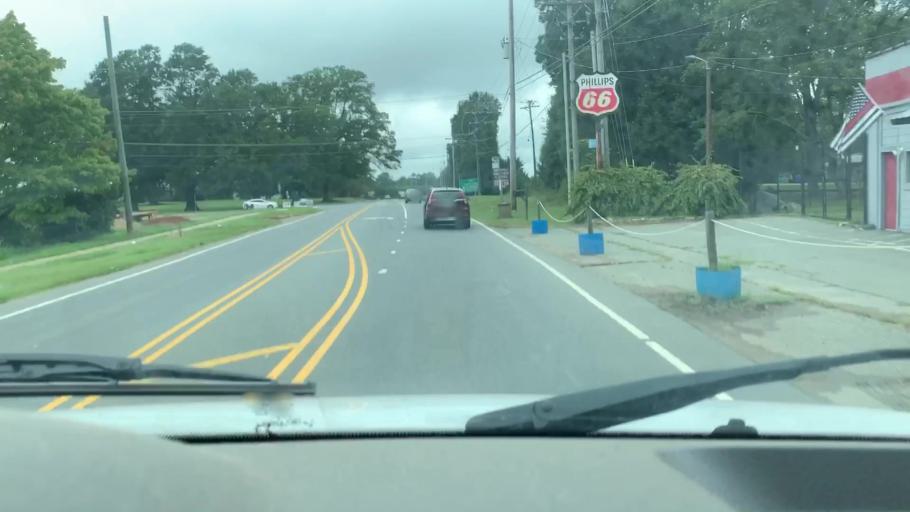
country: US
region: North Carolina
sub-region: Mecklenburg County
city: Huntersville
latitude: 35.3952
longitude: -80.8360
